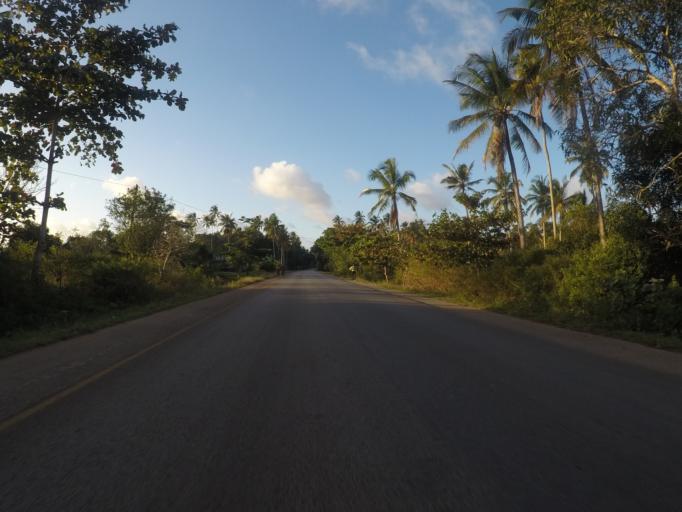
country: TZ
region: Zanzibar Central/South
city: Koani
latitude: -6.1595
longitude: 39.3298
